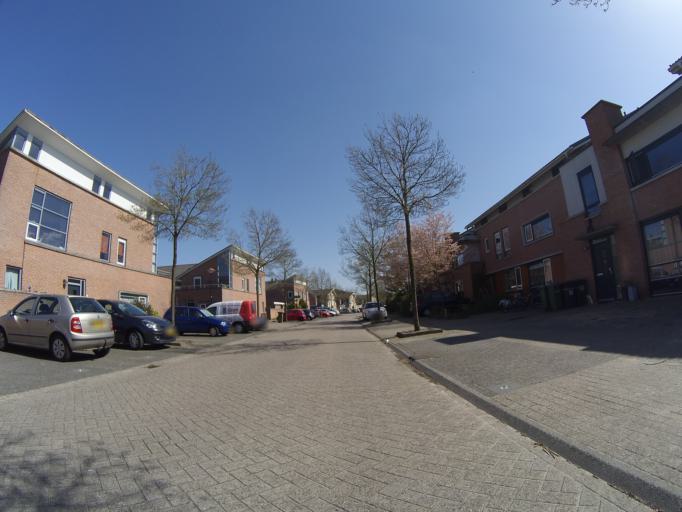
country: NL
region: Utrecht
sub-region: Gemeente Amersfoort
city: Hoogland
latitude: 52.2044
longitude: 5.3816
